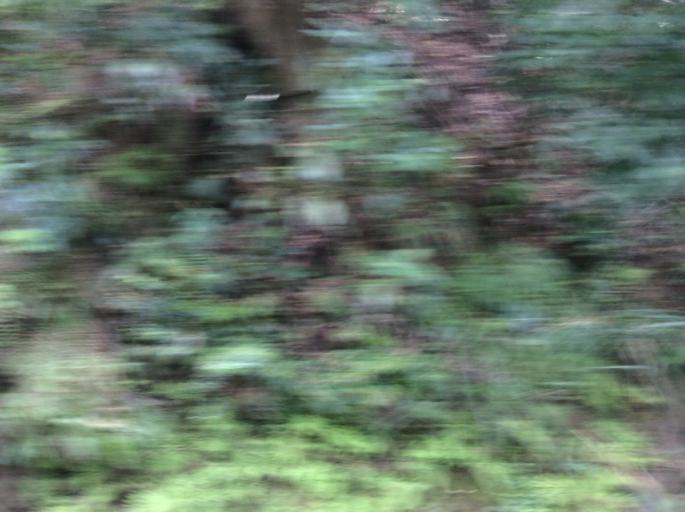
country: TW
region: Taipei
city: Taipei
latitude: 25.1665
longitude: 121.5415
